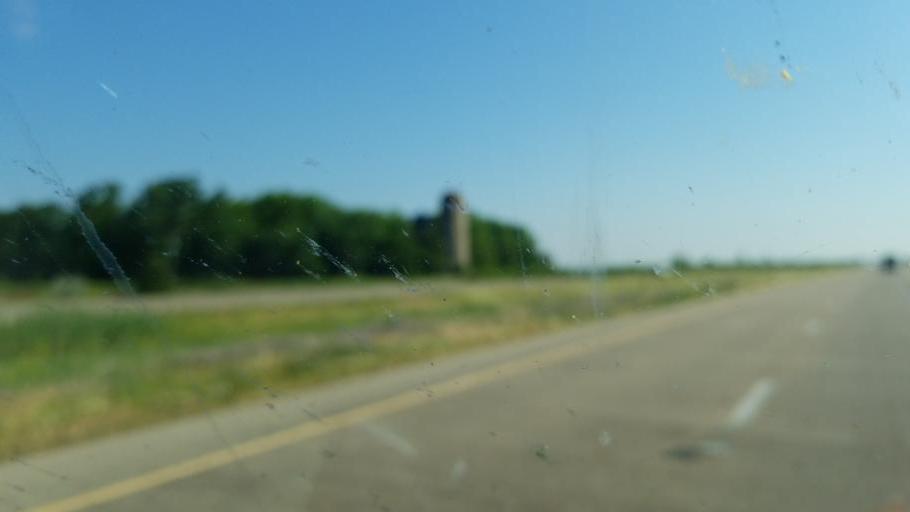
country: US
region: Illinois
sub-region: LaSalle County
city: Mendota
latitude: 41.4469
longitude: -89.0573
